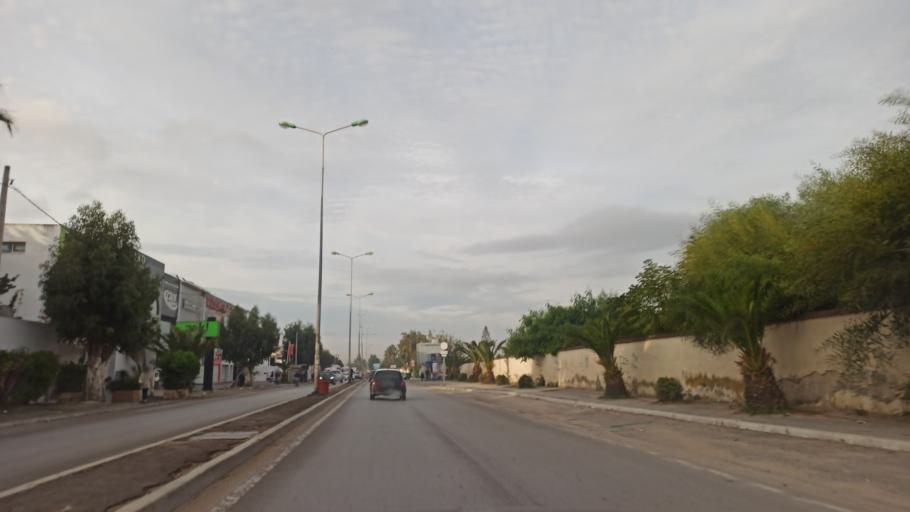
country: TN
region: Ariana
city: Ariana
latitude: 36.8744
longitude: 10.2398
